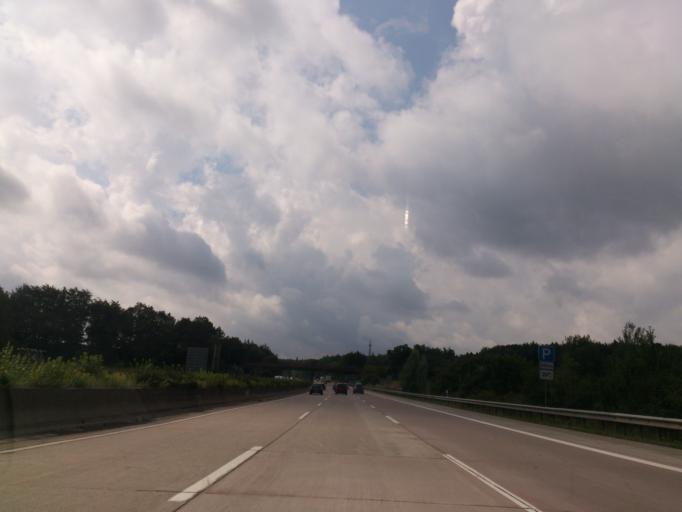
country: DE
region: Lower Saxony
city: Garlstorf
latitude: 53.2349
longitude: 10.0780
